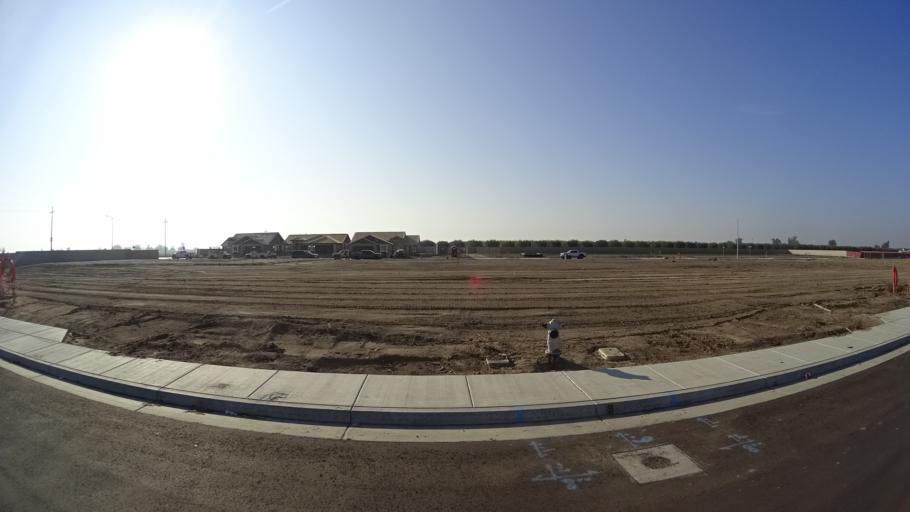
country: US
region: California
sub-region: Kern County
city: Greenfield
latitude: 35.2645
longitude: -119.0128
